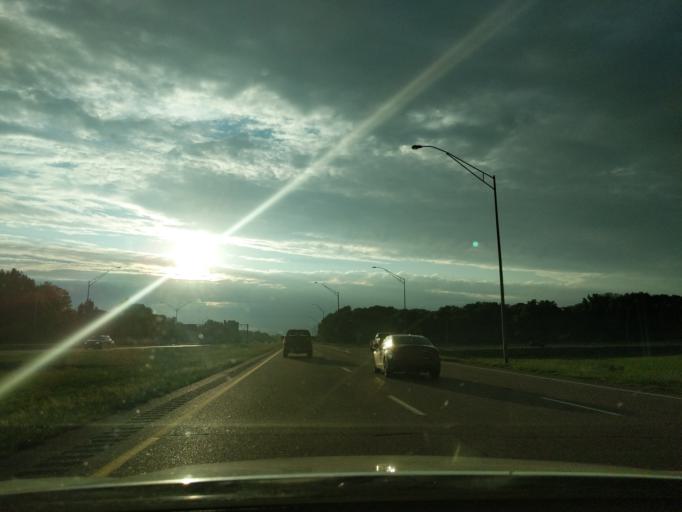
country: US
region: Tennessee
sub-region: Shelby County
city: New South Memphis
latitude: 35.0730
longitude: -90.0278
